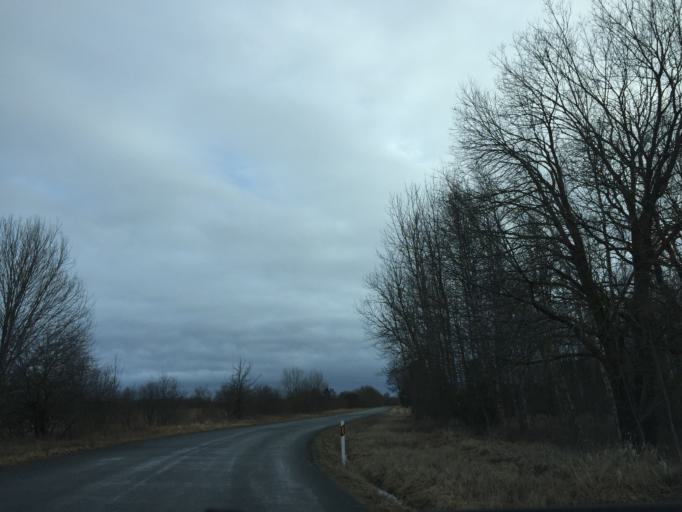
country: EE
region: Laeaene
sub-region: Haapsalu linn
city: Haapsalu
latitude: 58.8125
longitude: 23.5501
